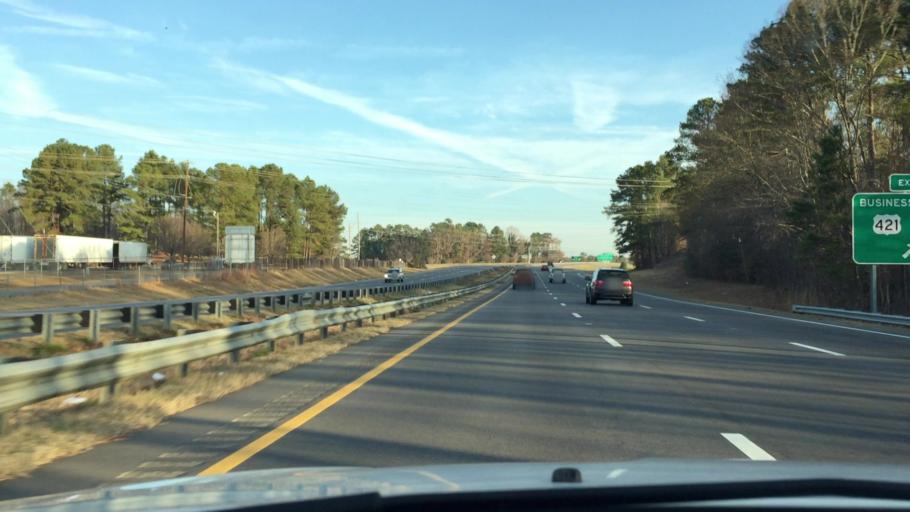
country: US
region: North Carolina
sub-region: Lee County
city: Sanford
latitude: 35.4903
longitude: -79.1967
